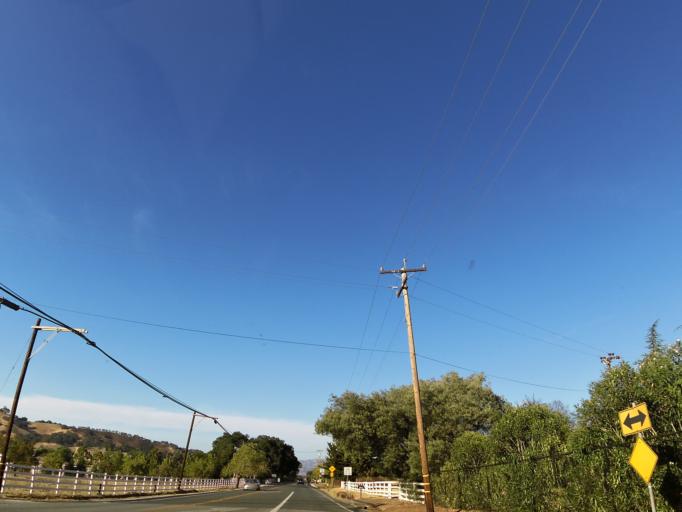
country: US
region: California
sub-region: Santa Clara County
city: San Martin
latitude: 37.0678
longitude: -121.6602
